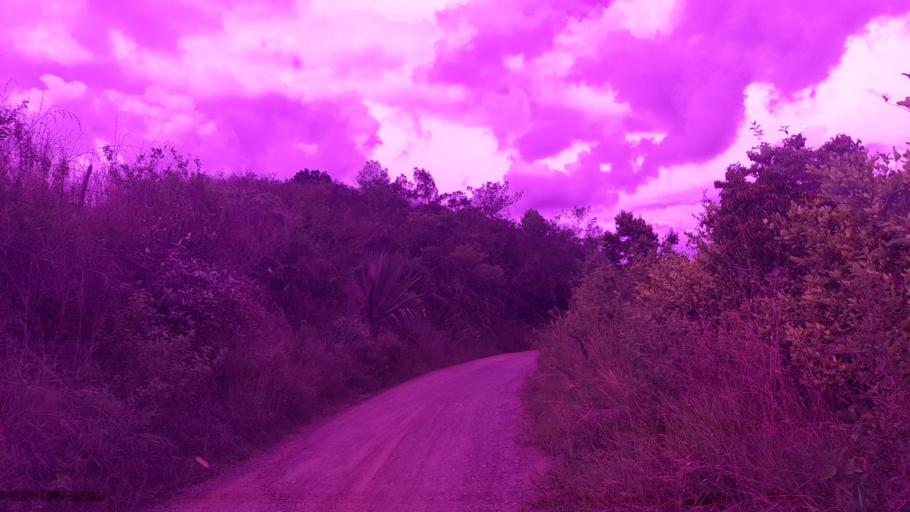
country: CO
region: Valle del Cauca
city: Andalucia
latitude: 4.1757
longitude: -76.1144
